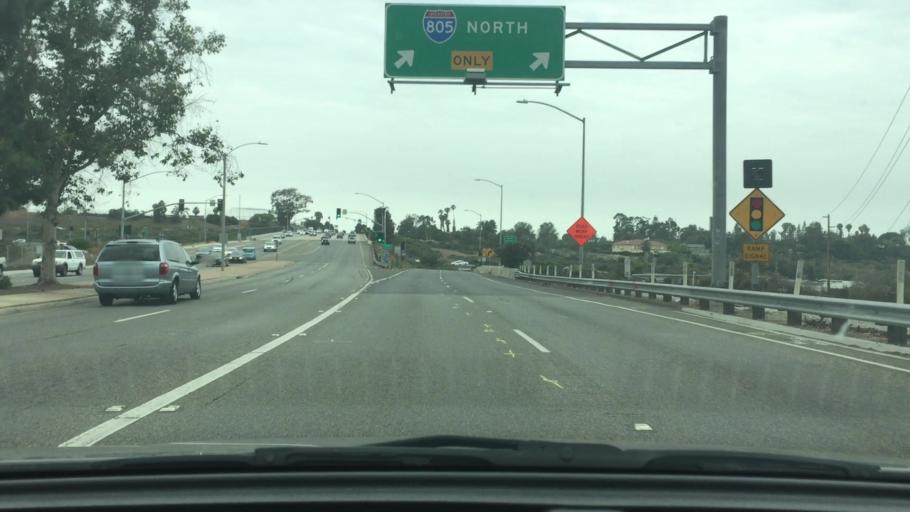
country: US
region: California
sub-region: San Diego County
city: Bonita
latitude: 32.6415
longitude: -117.0525
